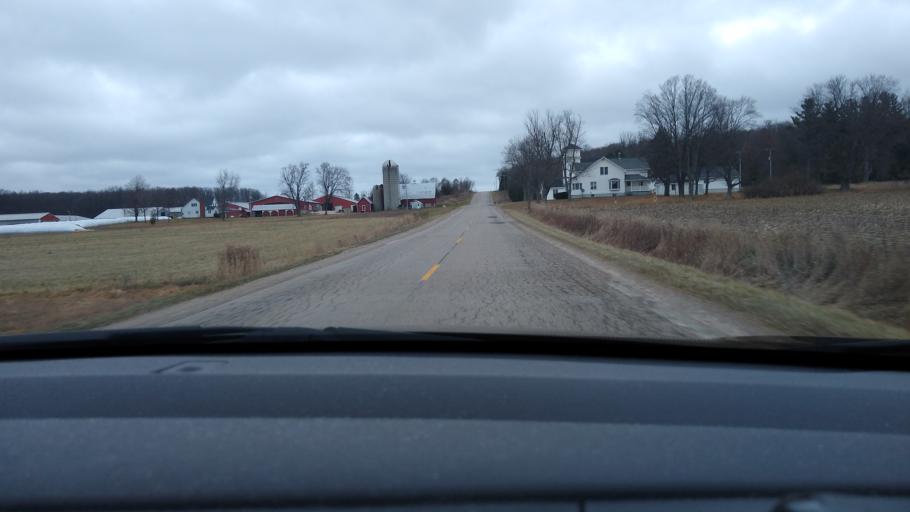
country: US
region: Michigan
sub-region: Missaukee County
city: Lake City
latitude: 44.2853
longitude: -85.0542
